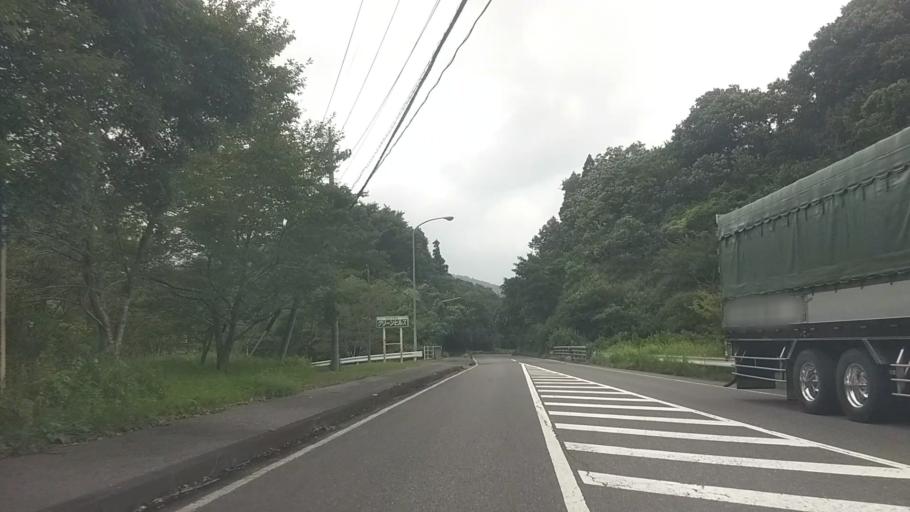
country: JP
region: Chiba
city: Kawaguchi
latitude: 35.2412
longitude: 140.0353
